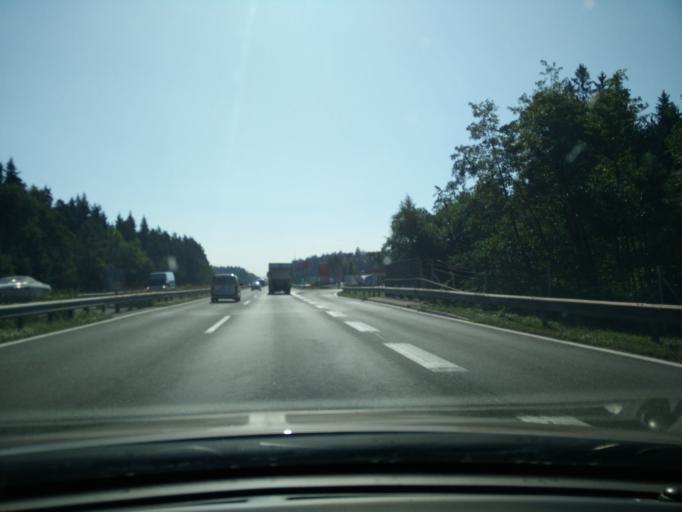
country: SI
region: Sencur
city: Sencur
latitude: 46.2295
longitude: 14.4176
